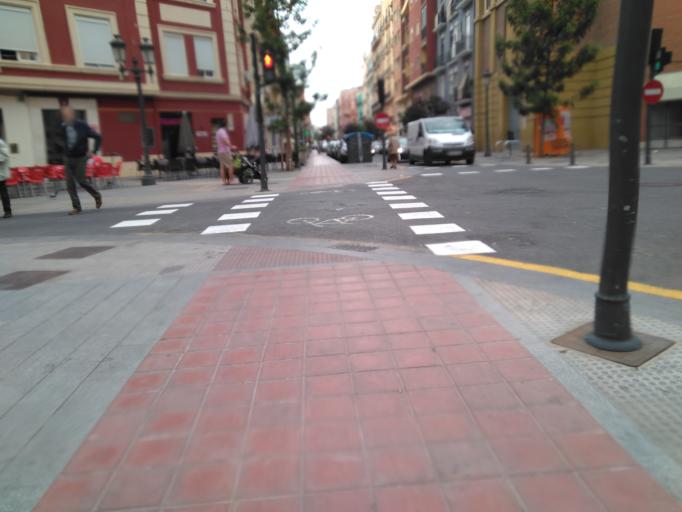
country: ES
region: Valencia
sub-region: Provincia de Valencia
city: Valencia
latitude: 39.4598
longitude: -0.3754
